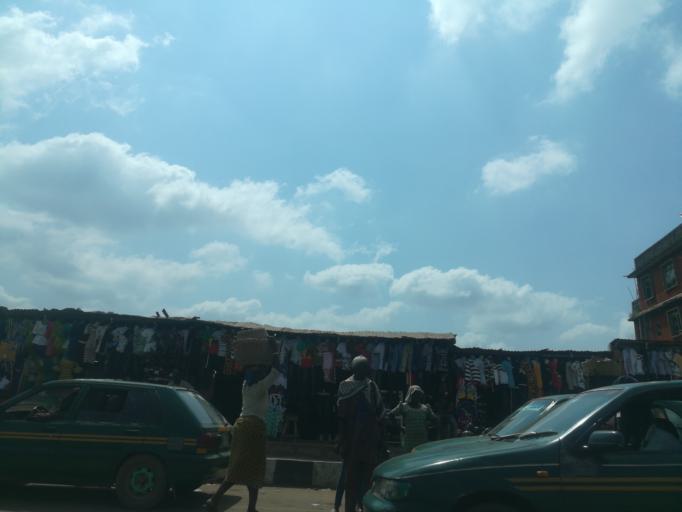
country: NG
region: Ogun
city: Abeokuta
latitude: 7.1558
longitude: 3.3280
